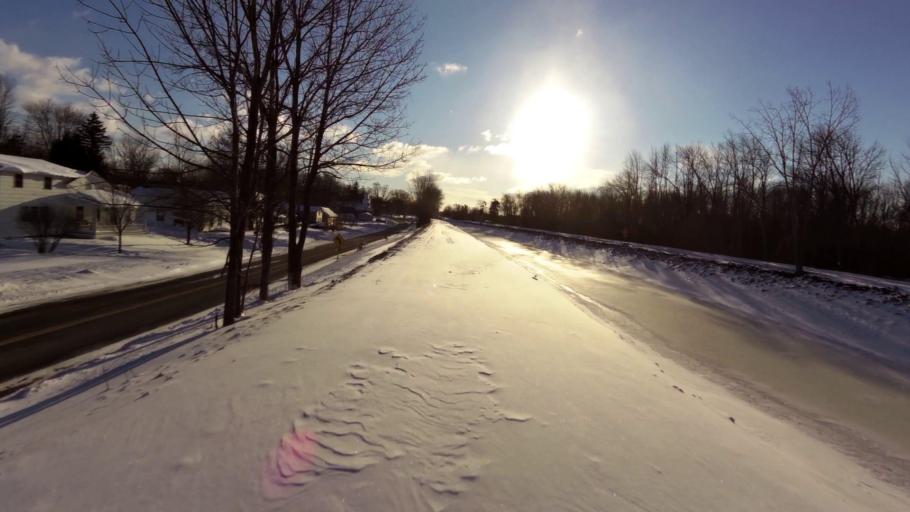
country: US
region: New York
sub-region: Orleans County
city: Albion
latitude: 43.2517
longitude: -78.2581
